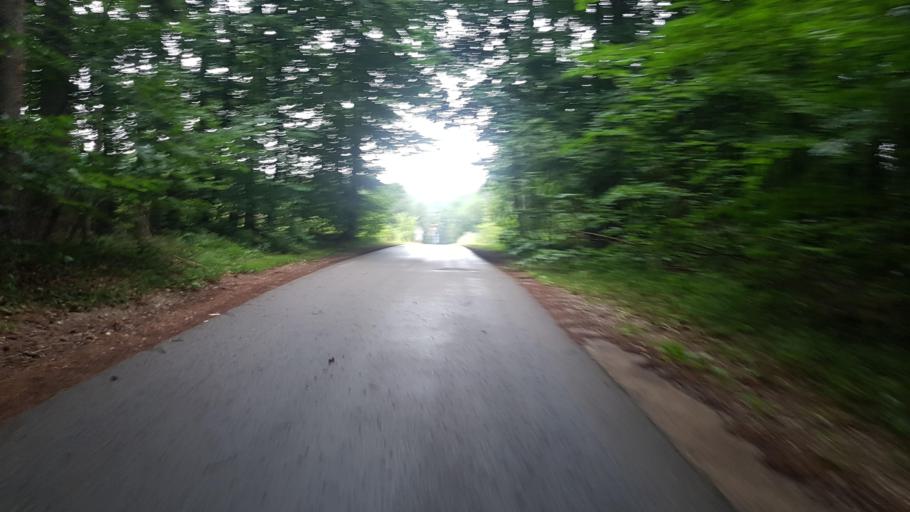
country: DE
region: Bavaria
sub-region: Upper Bavaria
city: Starnberg
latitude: 48.0192
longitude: 11.3471
